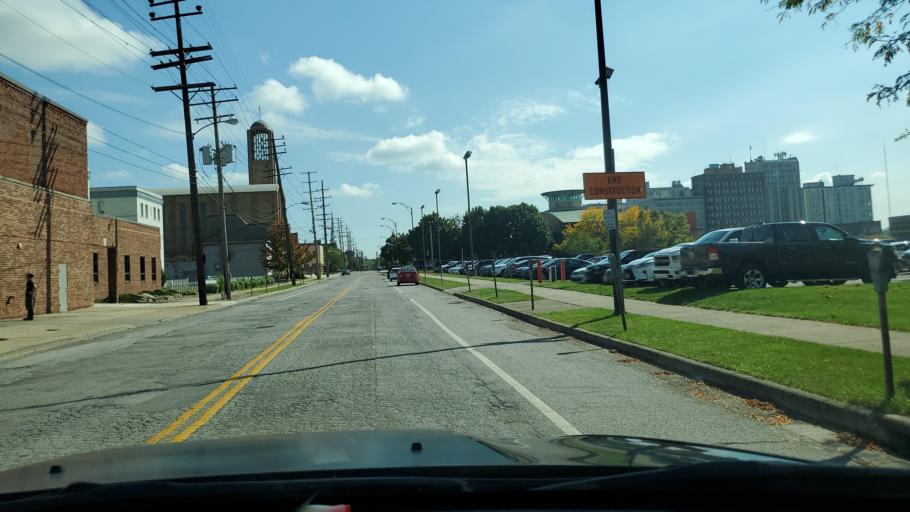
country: US
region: Ohio
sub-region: Mahoning County
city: Youngstown
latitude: 41.1038
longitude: -80.6528
